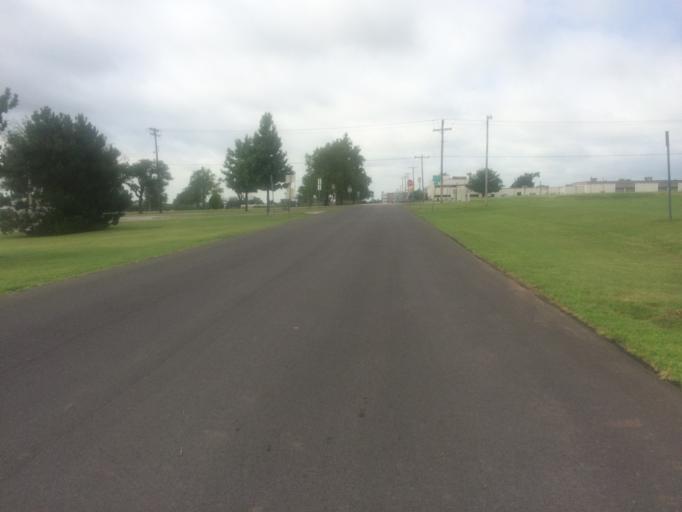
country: US
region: Oklahoma
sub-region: Cleveland County
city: Norman
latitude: 35.1921
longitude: -97.4396
